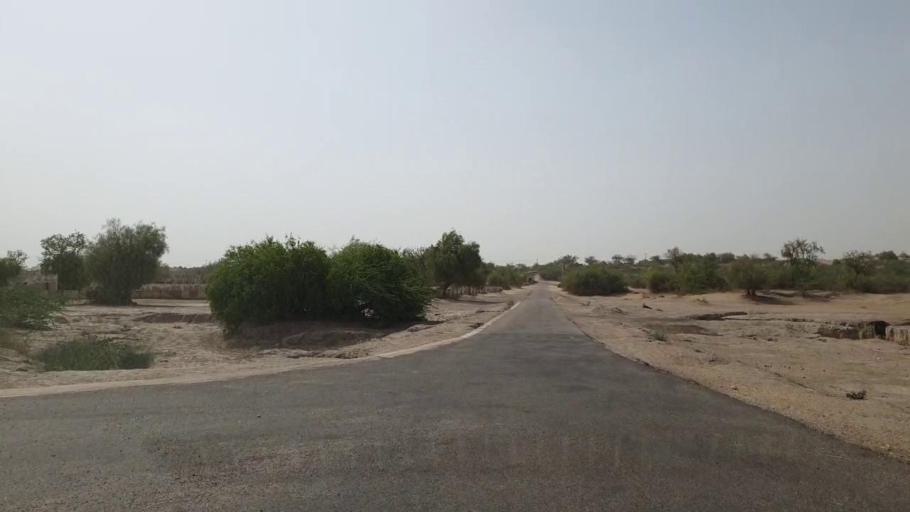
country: PK
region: Sindh
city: Mithi
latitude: 24.5738
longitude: 69.9301
